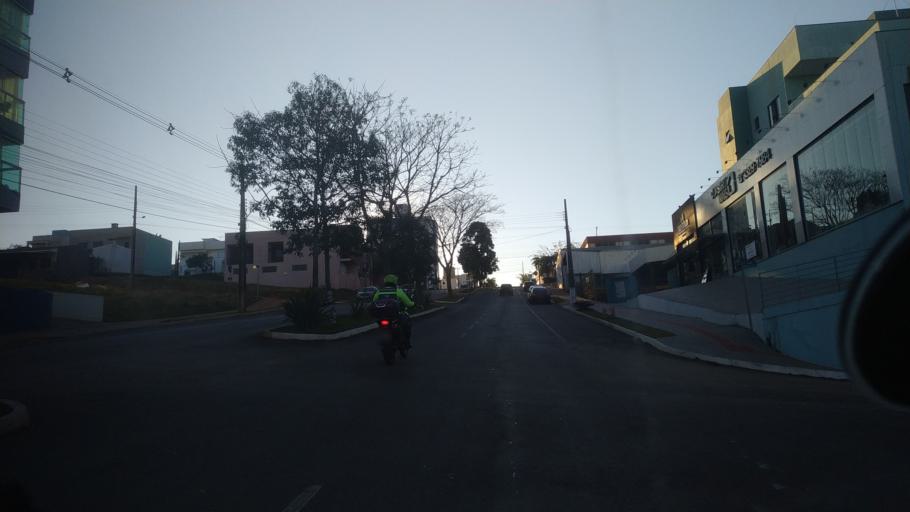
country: BR
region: Santa Catarina
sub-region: Chapeco
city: Chapeco
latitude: -27.0892
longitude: -52.5891
